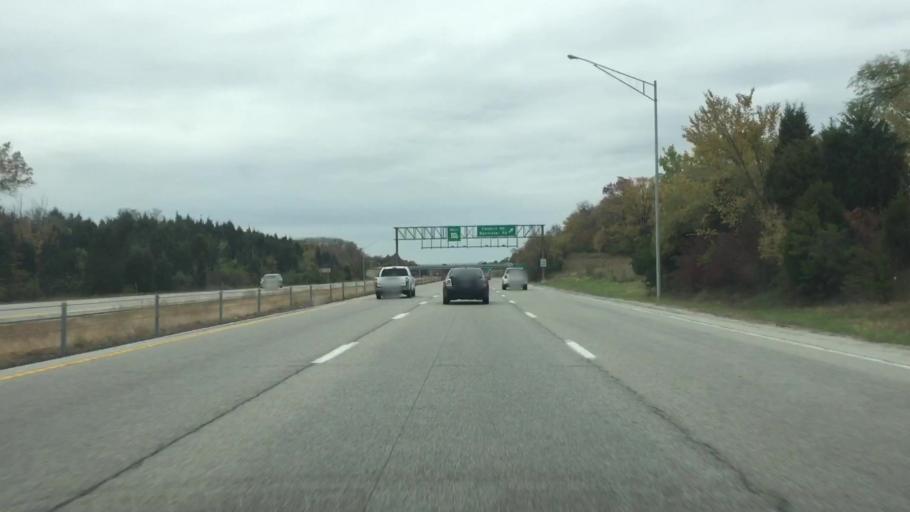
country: US
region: Missouri
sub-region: Jackson County
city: Lees Summit
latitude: 38.9389
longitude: -94.4075
